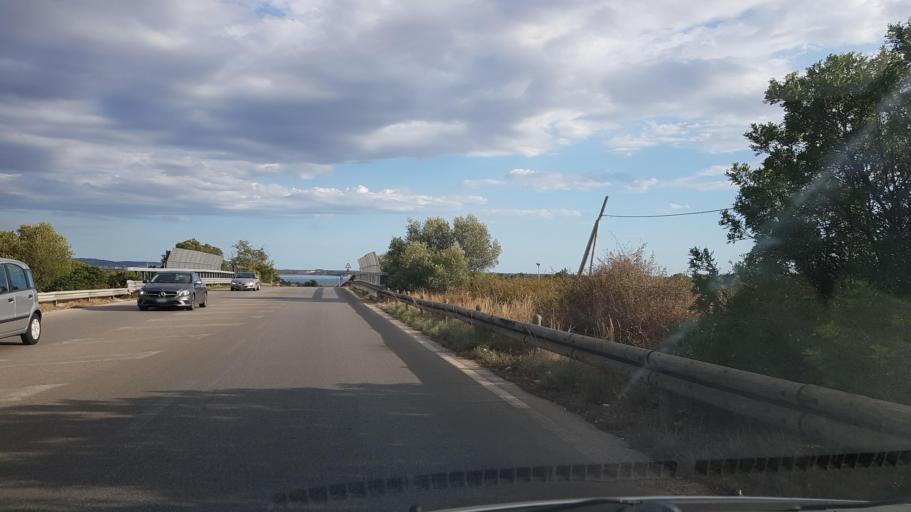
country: IT
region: Apulia
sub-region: Provincia di Taranto
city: Paolo VI
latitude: 40.5123
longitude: 17.2896
